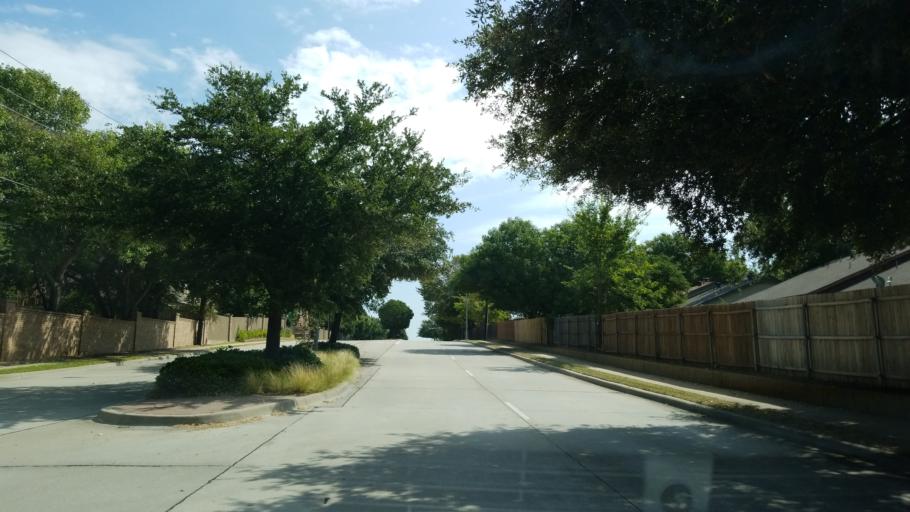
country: US
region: Texas
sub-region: Tarrant County
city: Euless
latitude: 32.8811
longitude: -97.0873
